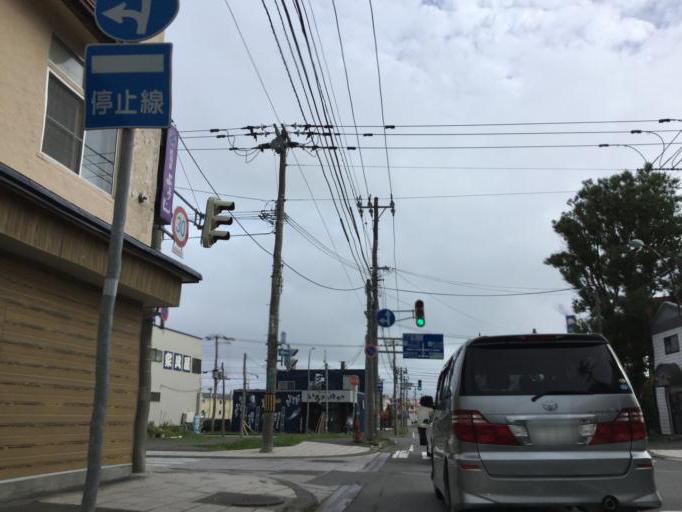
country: JP
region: Hokkaido
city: Wakkanai
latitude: 45.3971
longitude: 141.6872
